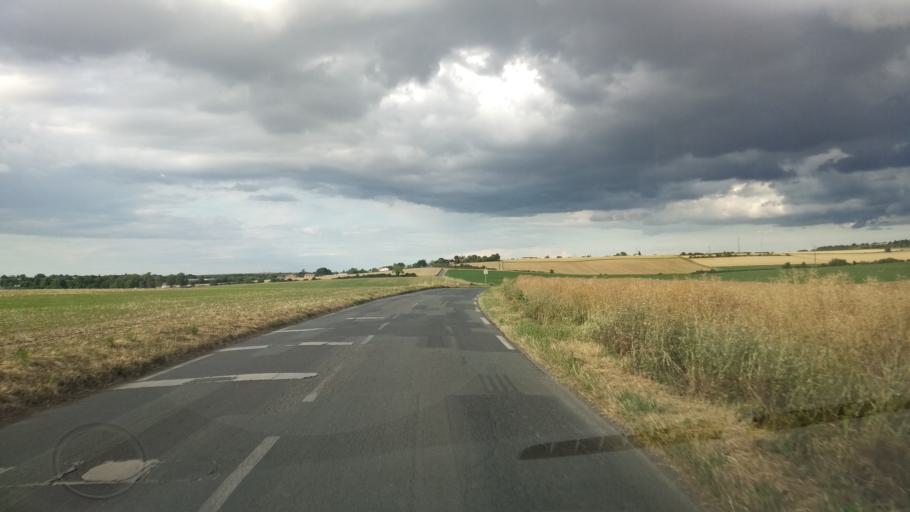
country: FR
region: Poitou-Charentes
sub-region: Departement de la Vienne
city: Migne-Auxances
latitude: 46.6206
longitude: 0.3212
